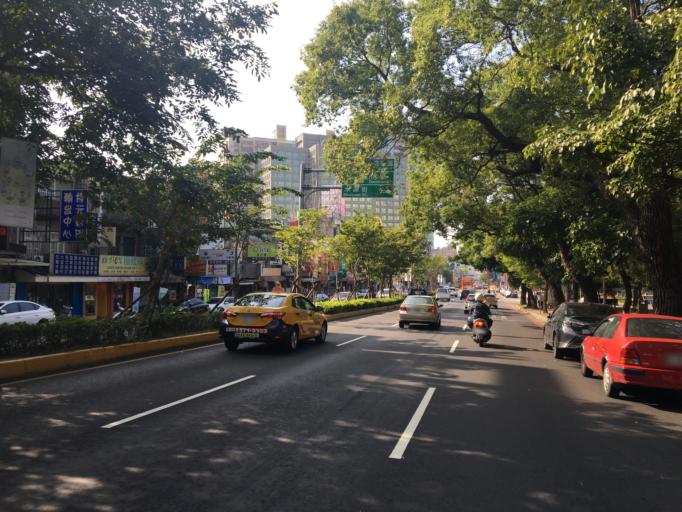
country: TW
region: Taiwan
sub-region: Hsinchu
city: Hsinchu
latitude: 24.7994
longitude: 120.9923
